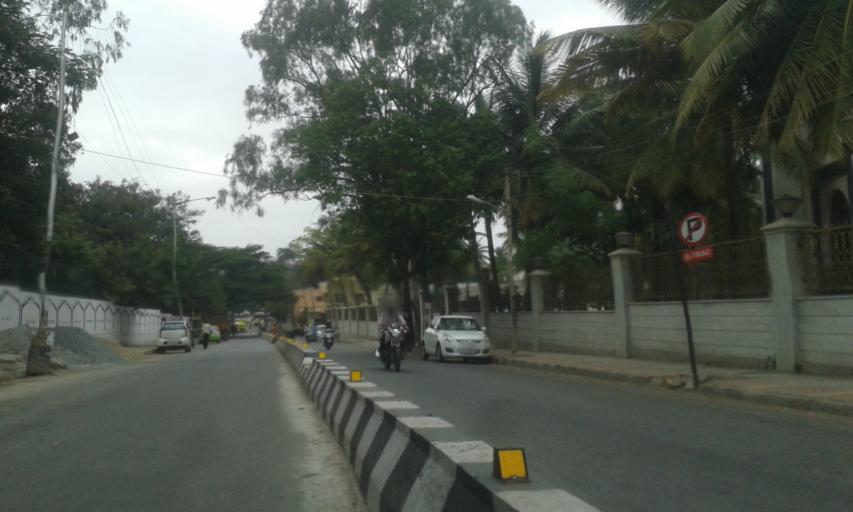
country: IN
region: Karnataka
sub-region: Bangalore Urban
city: Bangalore
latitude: 12.9205
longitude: 77.5998
